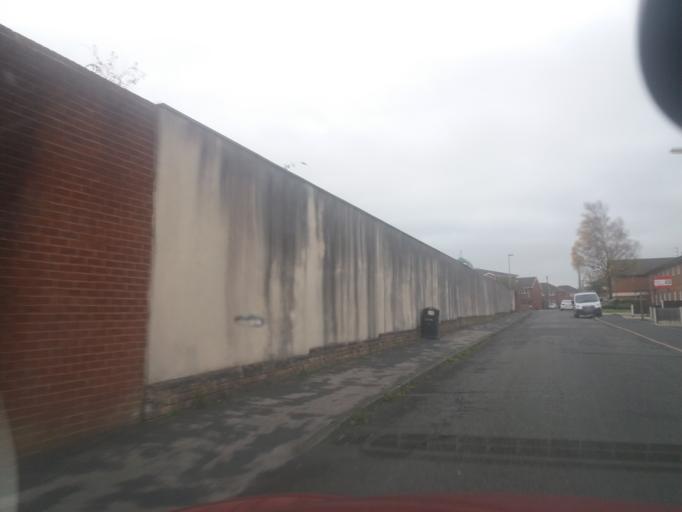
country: GB
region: England
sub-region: Lancashire
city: Chorley
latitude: 53.6504
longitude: -2.6232
